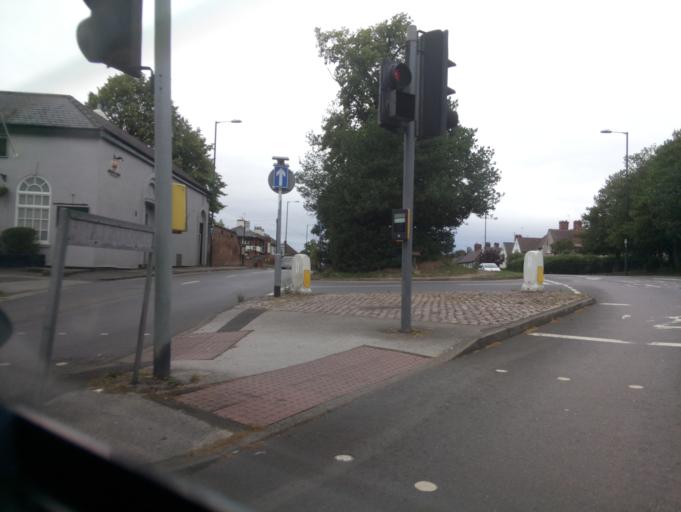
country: GB
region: England
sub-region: Nottinghamshire
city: Arnold
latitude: 52.9840
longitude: -1.1445
